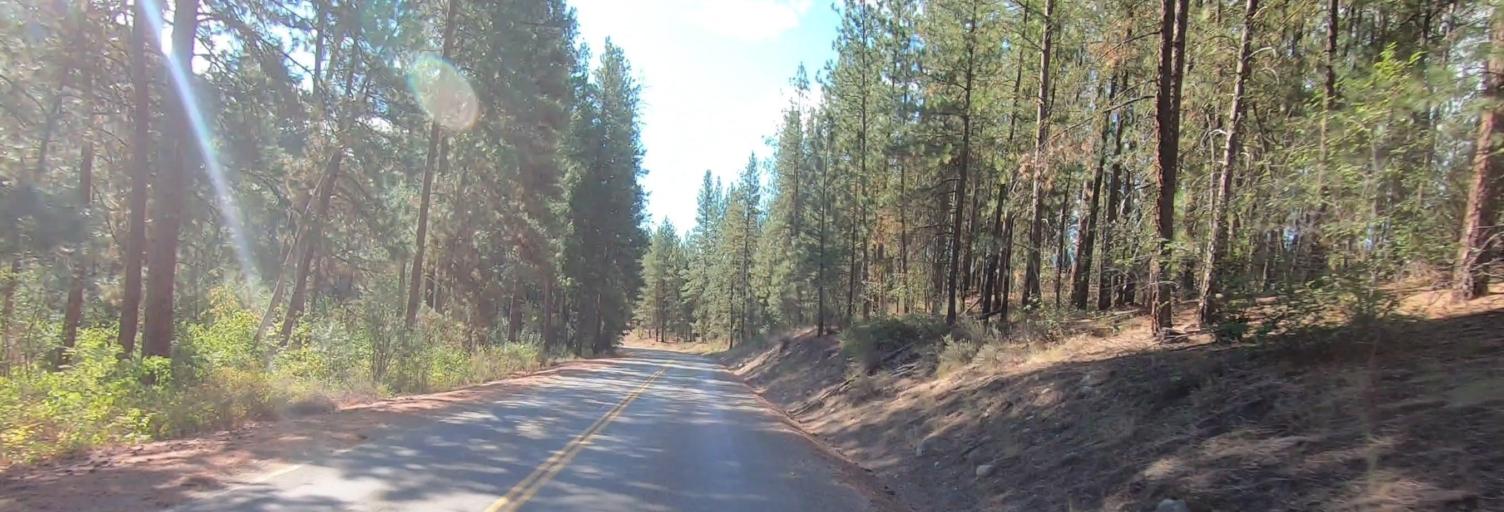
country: US
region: Washington
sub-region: Okanogan County
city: Brewster
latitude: 48.5421
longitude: -120.1796
